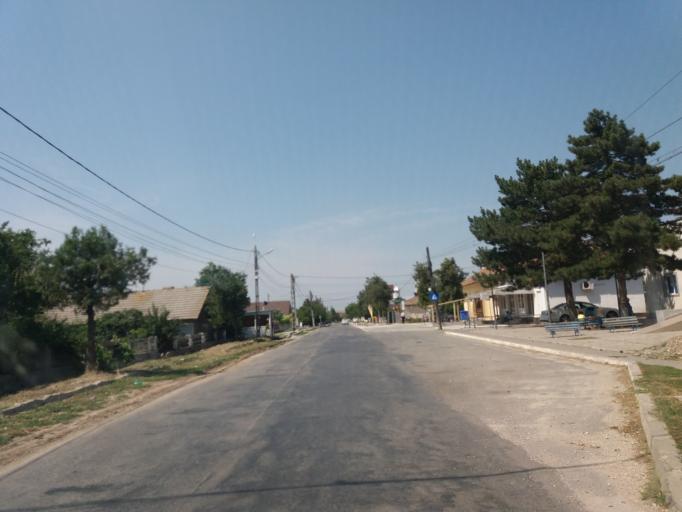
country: RO
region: Constanta
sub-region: Comuna Corbu
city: Corbu
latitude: 44.4120
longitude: 28.6614
